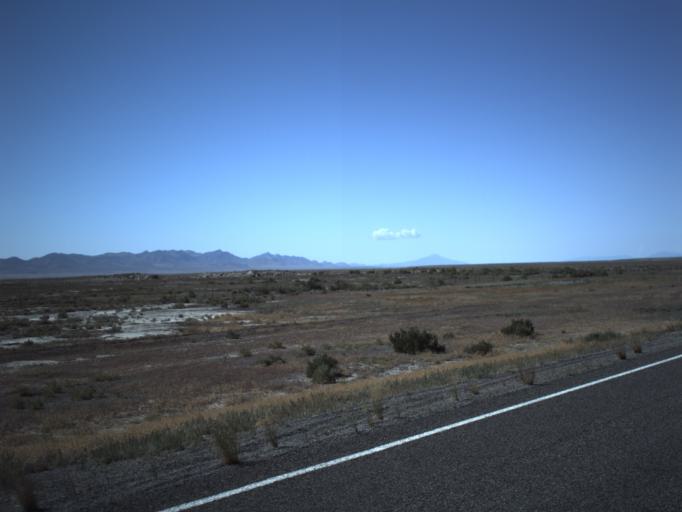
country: US
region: Utah
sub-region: Millard County
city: Delta
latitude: 39.2362
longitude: -112.9219
